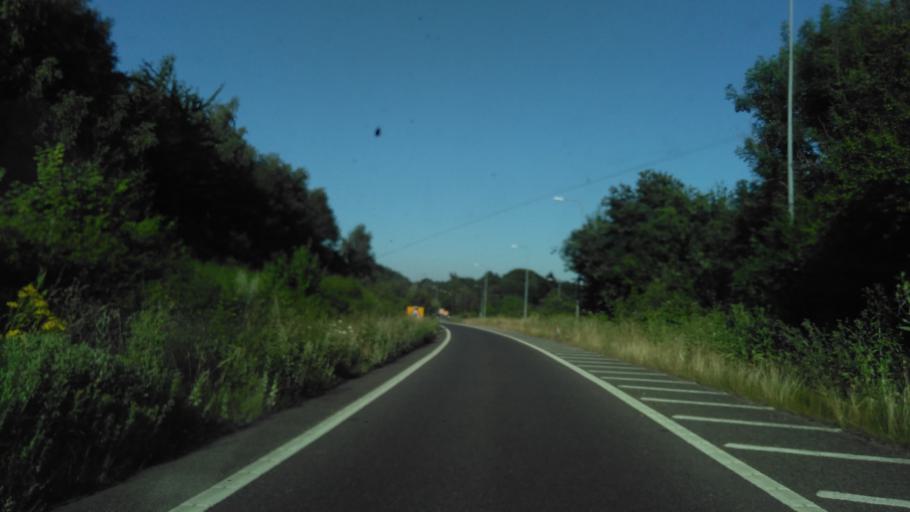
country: GB
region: England
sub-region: Kent
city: Blean
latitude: 51.2822
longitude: 1.0378
